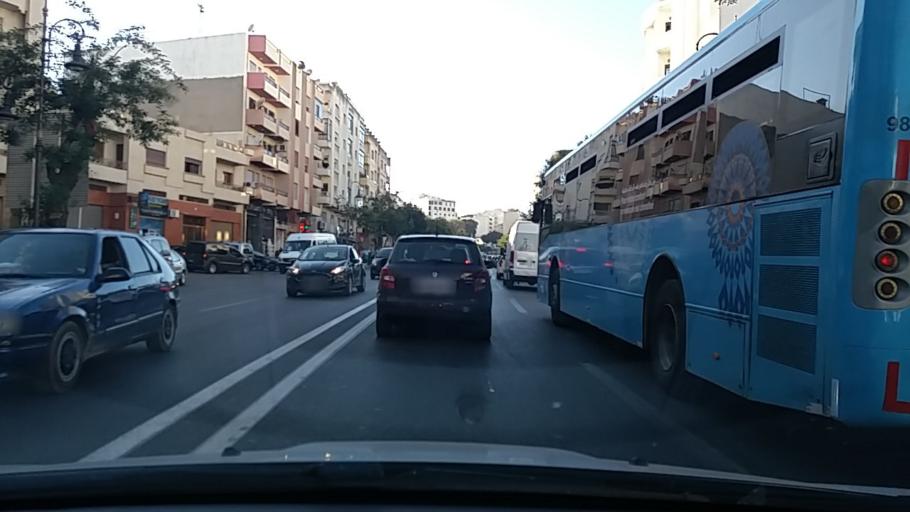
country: MA
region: Tanger-Tetouan
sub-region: Tanger-Assilah
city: Tangier
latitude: 35.7738
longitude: -5.8169
